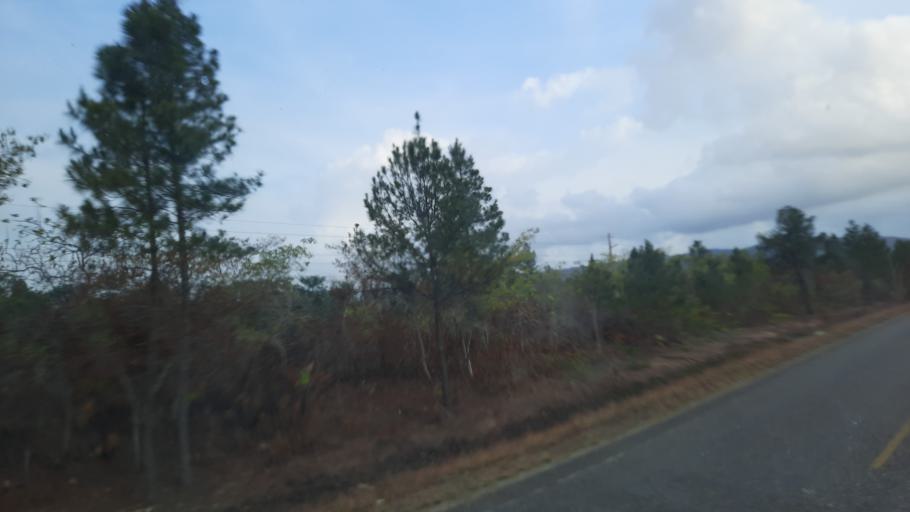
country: BZ
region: Stann Creek
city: Placencia
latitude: 16.6845
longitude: -88.4382
